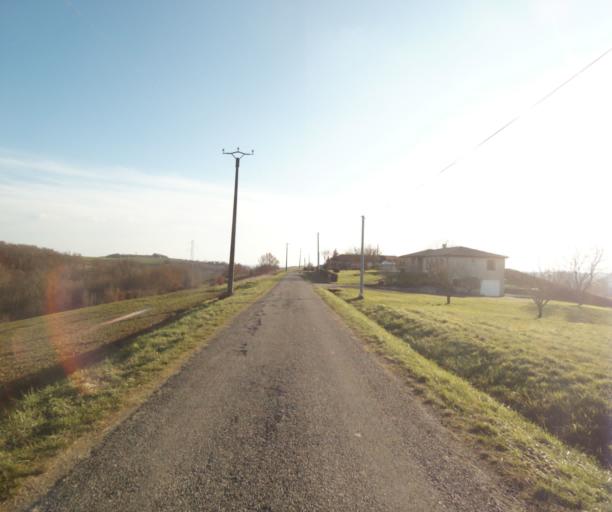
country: FR
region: Midi-Pyrenees
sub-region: Departement du Tarn-et-Garonne
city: Moissac
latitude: 44.1412
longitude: 1.1116
